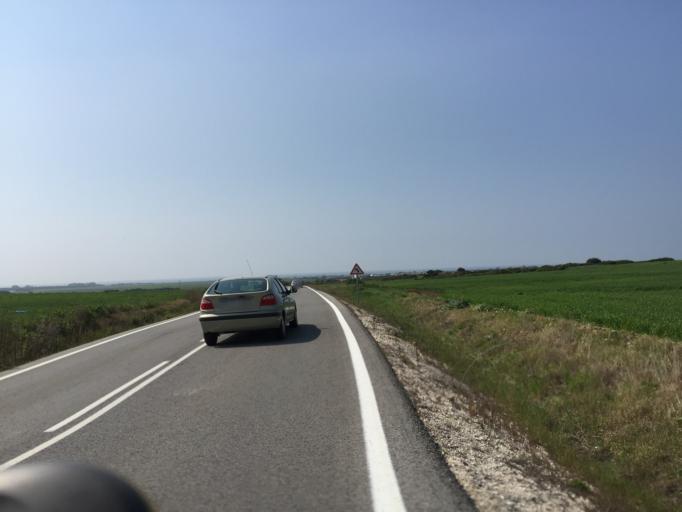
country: ES
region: Andalusia
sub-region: Provincia de Cadiz
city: Conil de la Frontera
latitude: 36.2293
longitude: -6.0379
